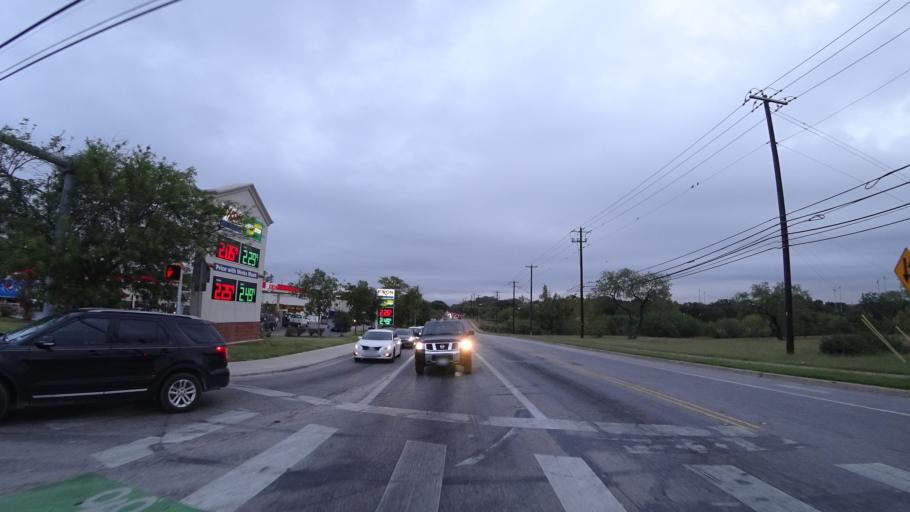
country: US
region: Texas
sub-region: Travis County
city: Austin
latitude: 30.3040
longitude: -97.6990
